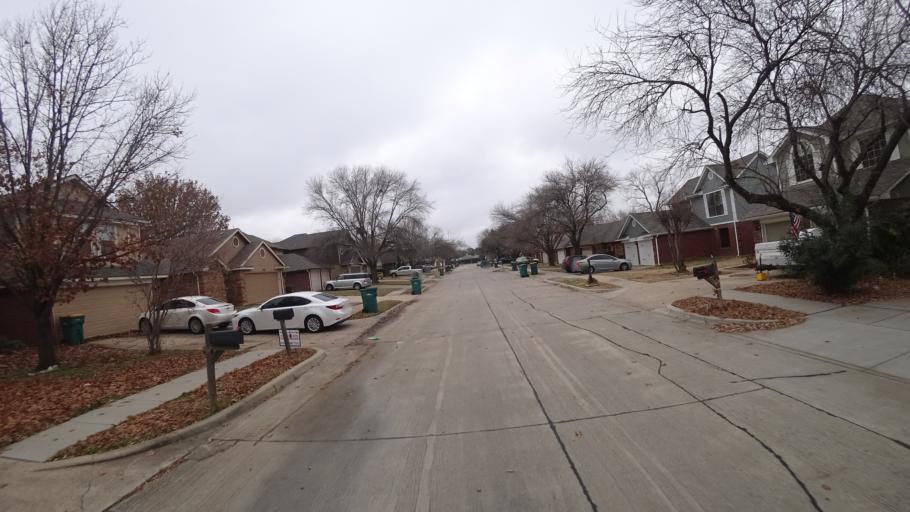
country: US
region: Texas
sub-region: Denton County
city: Lewisville
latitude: 33.0340
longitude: -97.0298
